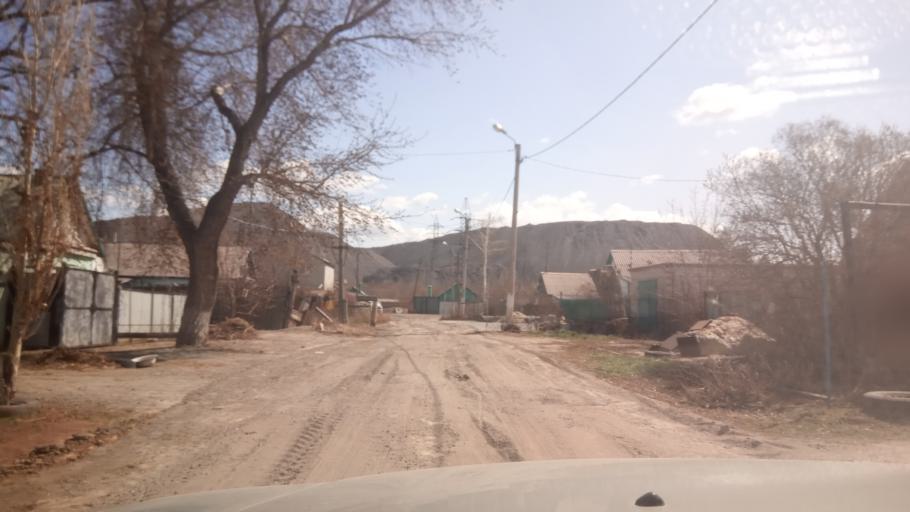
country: RU
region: Orenburg
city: Novotroitsk
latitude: 51.2122
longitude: 58.3155
